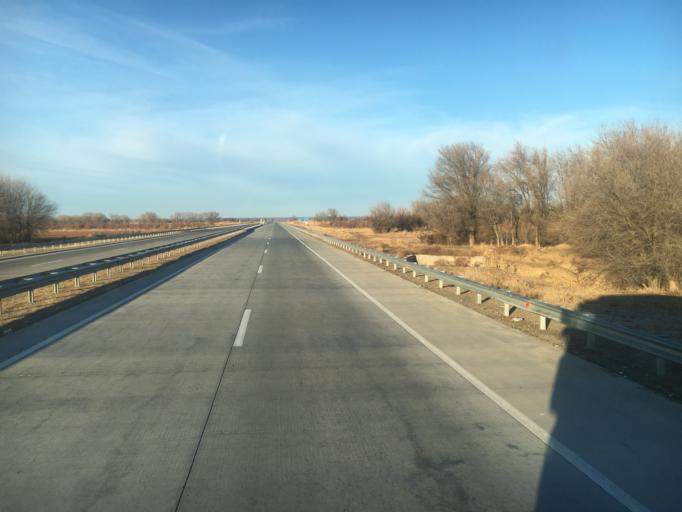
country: KZ
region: Ongtustik Qazaqstan
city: Turkestan
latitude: 43.1555
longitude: 68.5648
